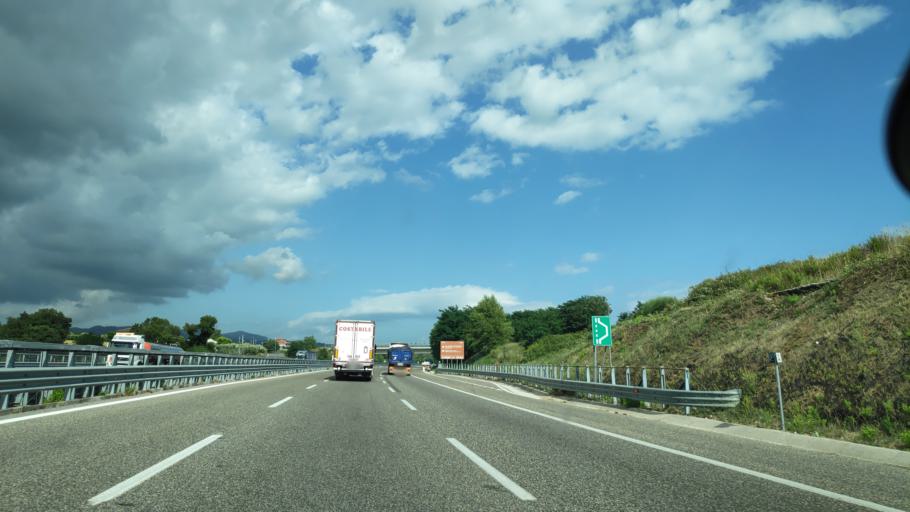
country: IT
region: Campania
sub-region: Provincia di Salerno
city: Contursi Terme
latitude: 40.6149
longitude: 15.2728
